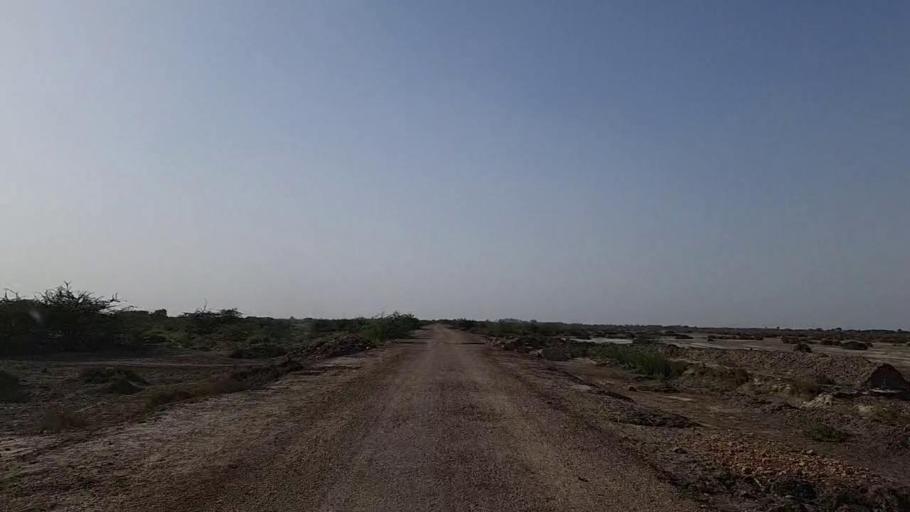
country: PK
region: Sindh
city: Jati
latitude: 24.2824
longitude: 68.2257
